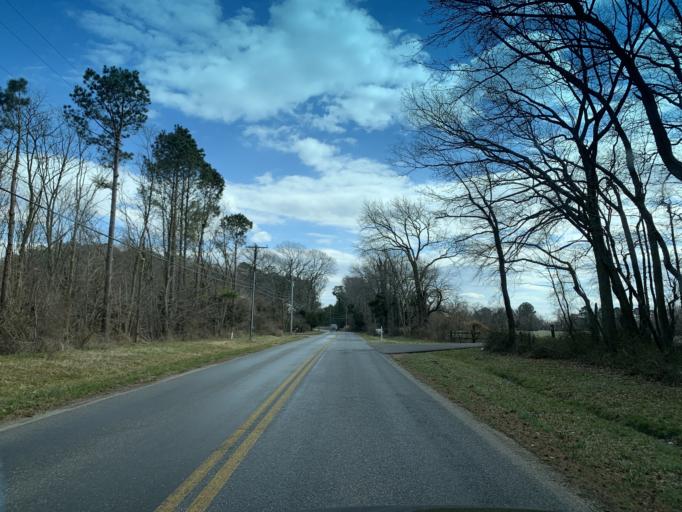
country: US
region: Maryland
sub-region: Queen Anne's County
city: Chester
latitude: 38.9475
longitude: -76.2712
